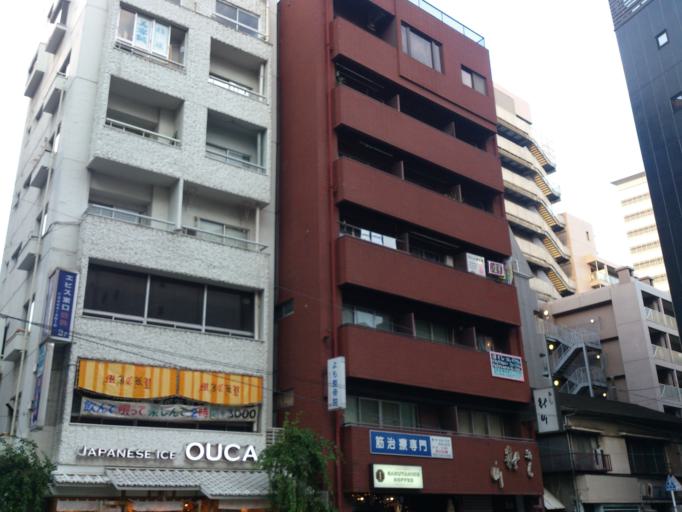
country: JP
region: Tokyo
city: Tokyo
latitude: 35.6474
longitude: 139.7106
